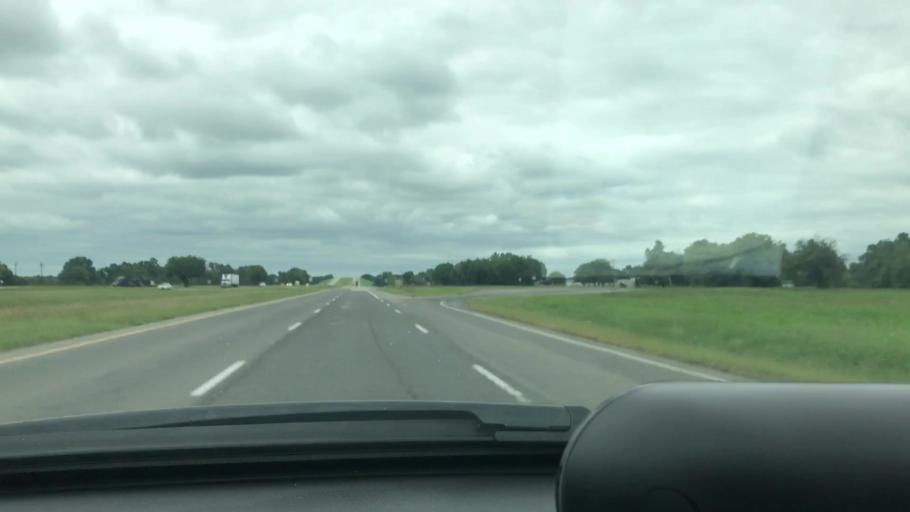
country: US
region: Oklahoma
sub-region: Wagoner County
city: Wagoner
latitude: 35.8689
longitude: -95.4024
